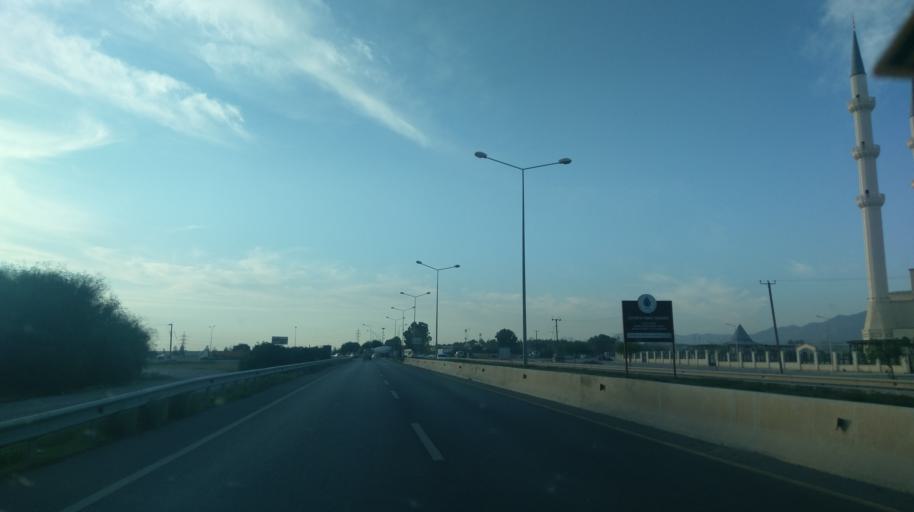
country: CY
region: Lefkosia
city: Nicosia
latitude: 35.2164
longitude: 33.4250
